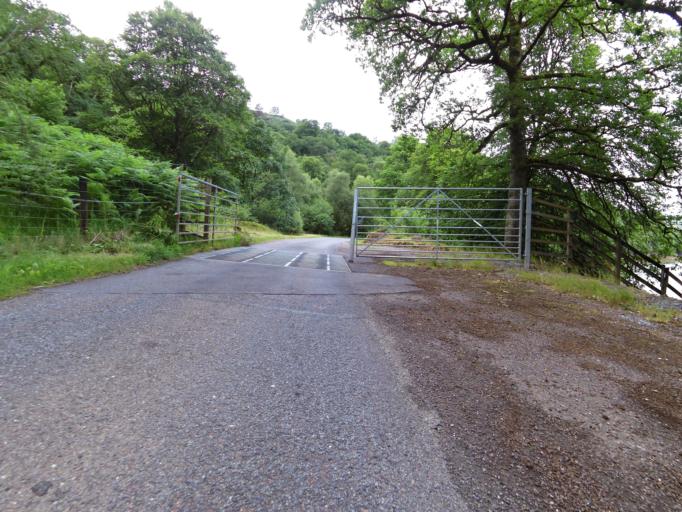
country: GB
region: Scotland
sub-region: Highland
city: Fort William
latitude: 56.8281
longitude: -5.1249
